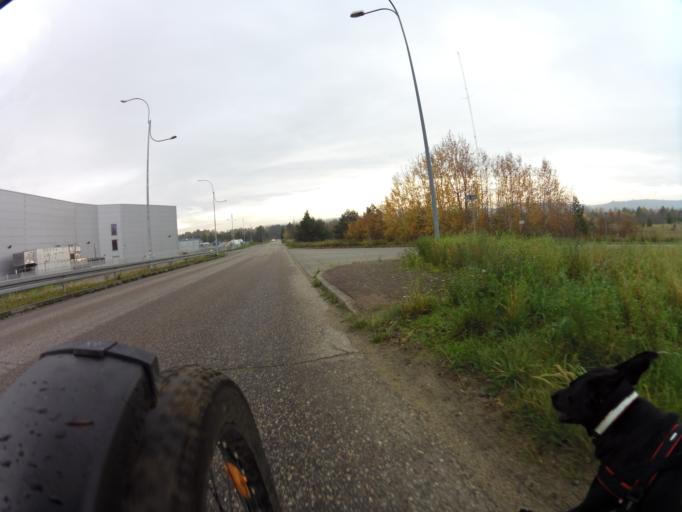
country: PL
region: Pomeranian Voivodeship
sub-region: Powiat pucki
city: Krokowa
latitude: 54.7385
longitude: 18.0942
